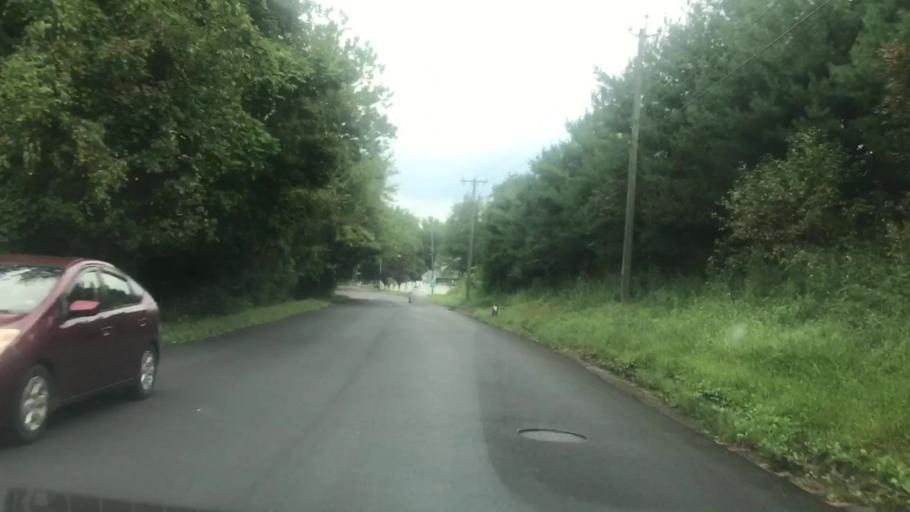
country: US
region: Connecticut
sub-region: Litchfield County
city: New Milford
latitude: 41.5799
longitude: -73.4170
